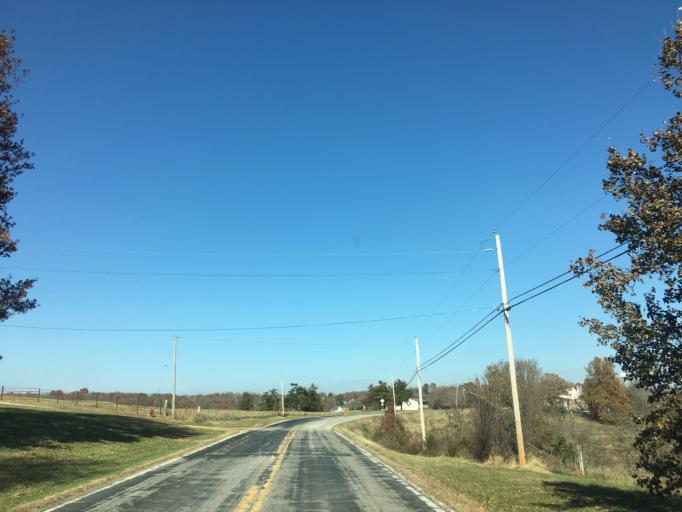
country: US
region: Missouri
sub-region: Cole County
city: Wardsville
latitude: 38.4739
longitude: -92.1779
